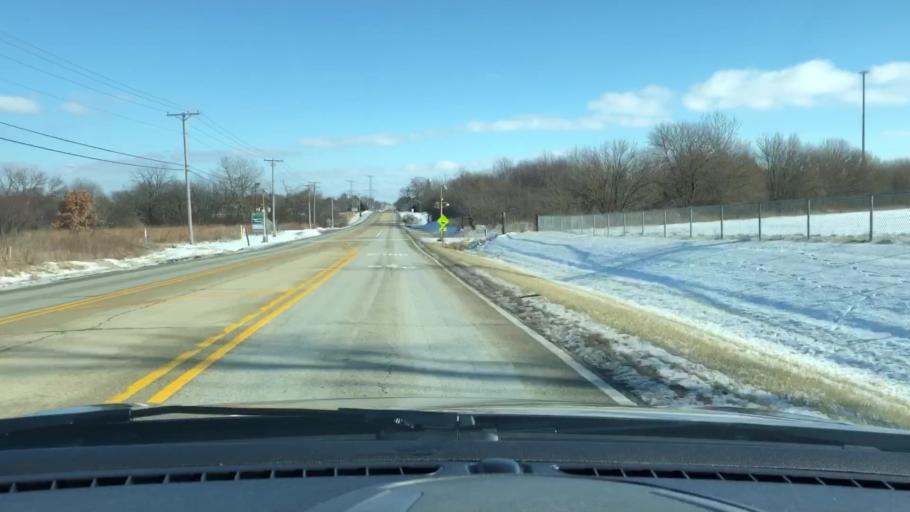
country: US
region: Illinois
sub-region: Will County
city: Preston Heights
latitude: 41.4816
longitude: -88.0439
